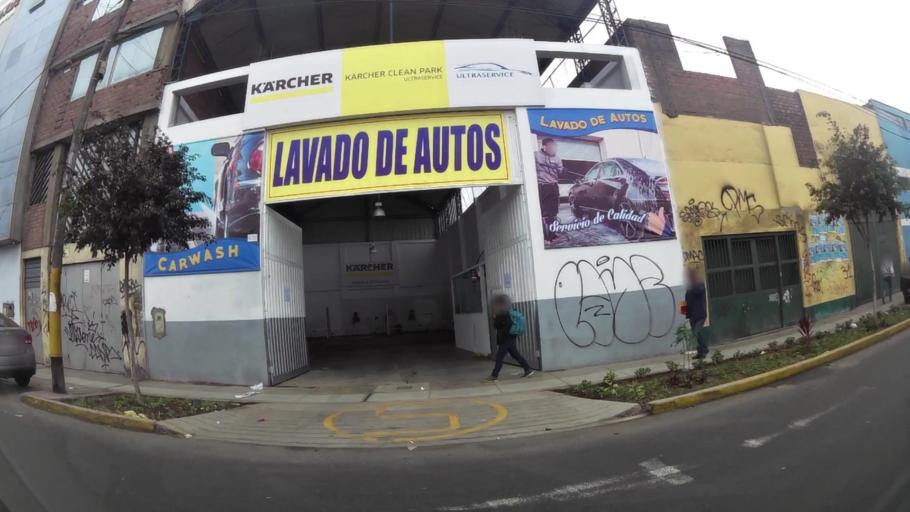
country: PE
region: Lima
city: Lima
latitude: -12.0529
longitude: -77.0556
